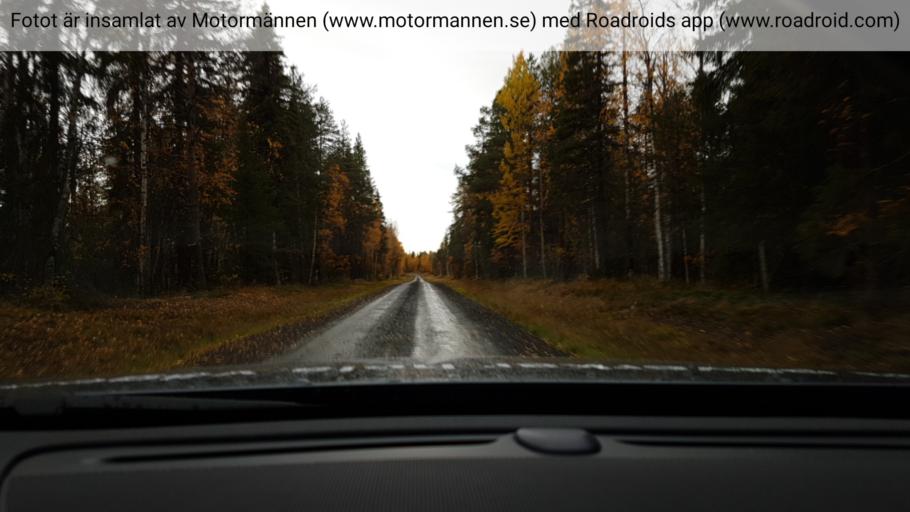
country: SE
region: Norrbotten
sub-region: Pajala Kommun
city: Pajala
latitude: 67.0936
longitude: 22.7421
